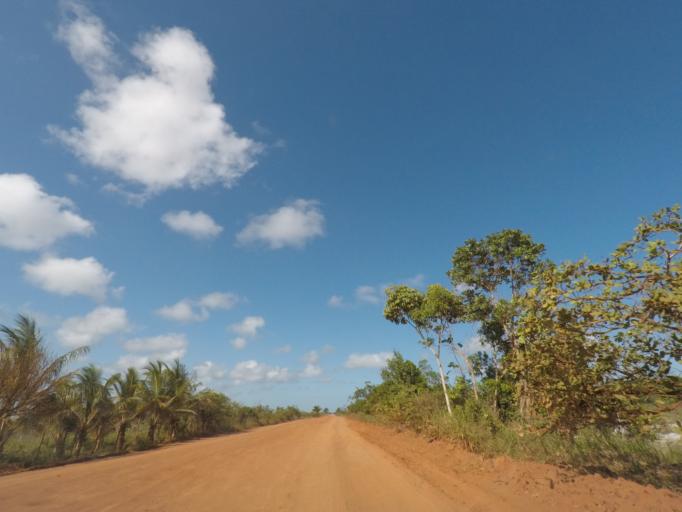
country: BR
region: Bahia
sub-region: Marau
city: Marau
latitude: -14.1756
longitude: -39.0203
